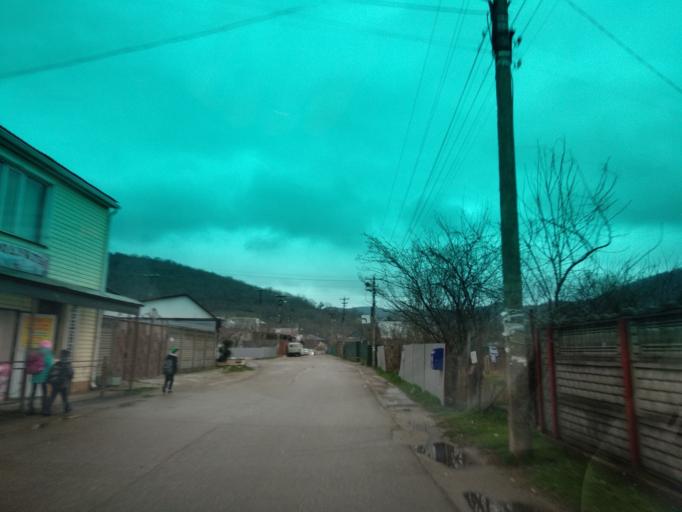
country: RU
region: Krasnodarskiy
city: Novomikhaylovskiy
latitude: 44.2612
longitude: 38.8626
